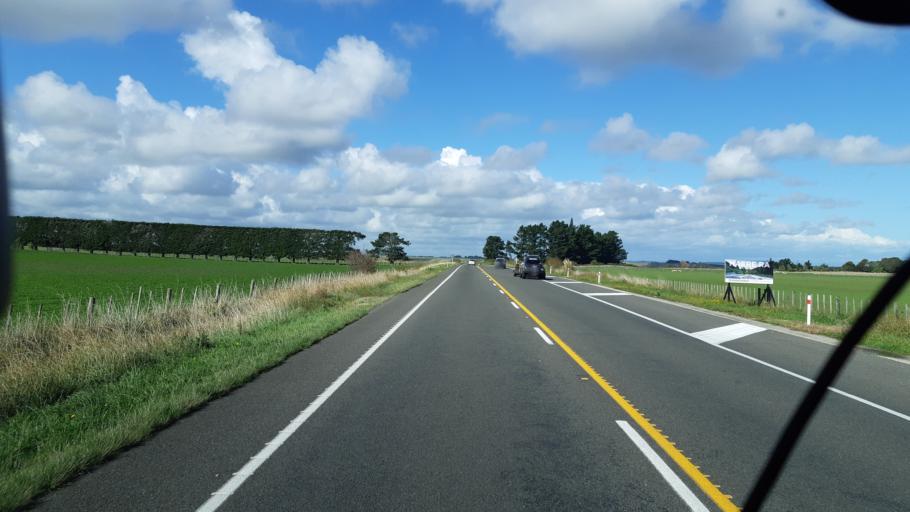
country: NZ
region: Manawatu-Wanganui
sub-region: Wanganui District
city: Wanganui
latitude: -39.9917
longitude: 175.1651
